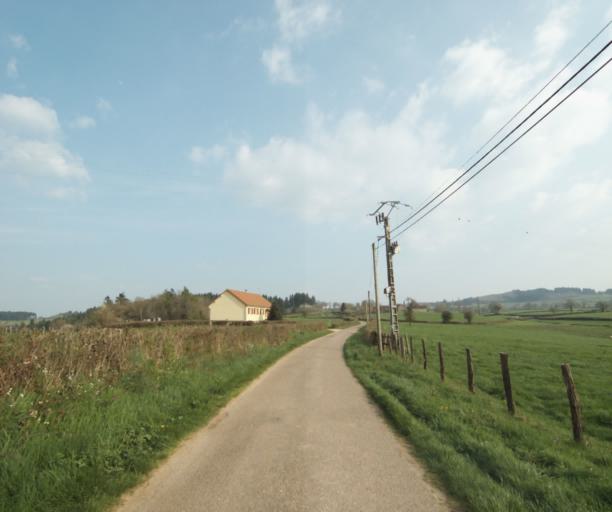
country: FR
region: Bourgogne
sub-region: Departement de Saone-et-Loire
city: Matour
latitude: 46.4689
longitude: 4.4697
